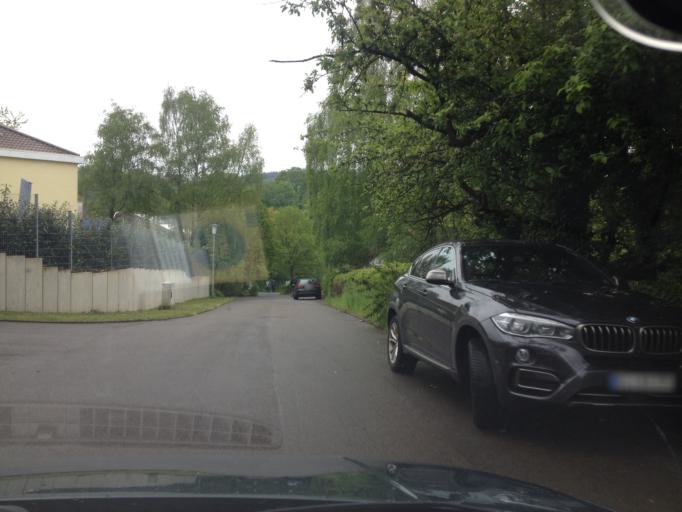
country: DE
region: Saarland
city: Sankt Wendel
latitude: 49.4651
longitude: 7.1808
